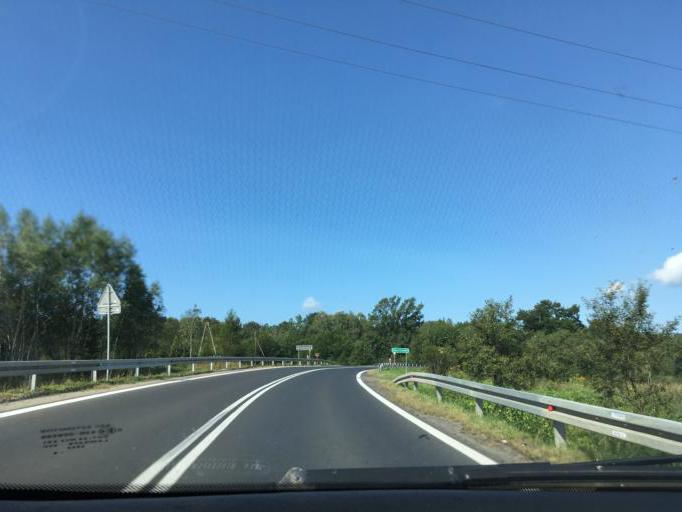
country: PL
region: Subcarpathian Voivodeship
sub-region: Powiat leski
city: Uherce Mineralne
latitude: 49.4661
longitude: 22.3888
